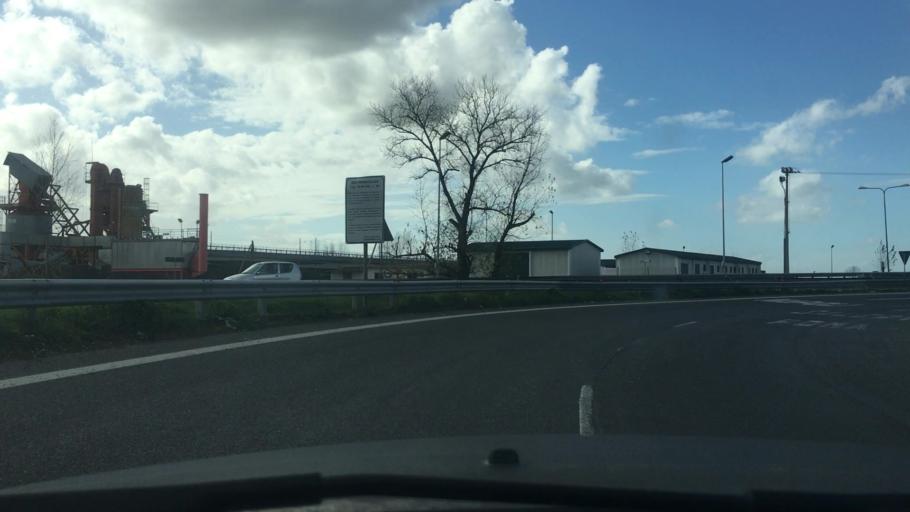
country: IT
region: Campania
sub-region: Provincia di Caserta
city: San Marco Evangelista
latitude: 41.0161
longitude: 14.3242
